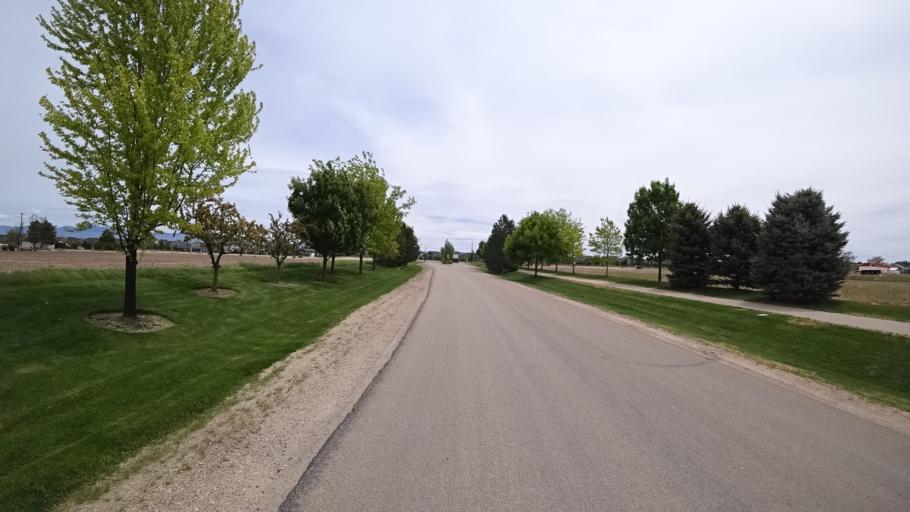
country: US
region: Idaho
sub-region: Ada County
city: Meridian
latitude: 43.5535
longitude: -116.3566
